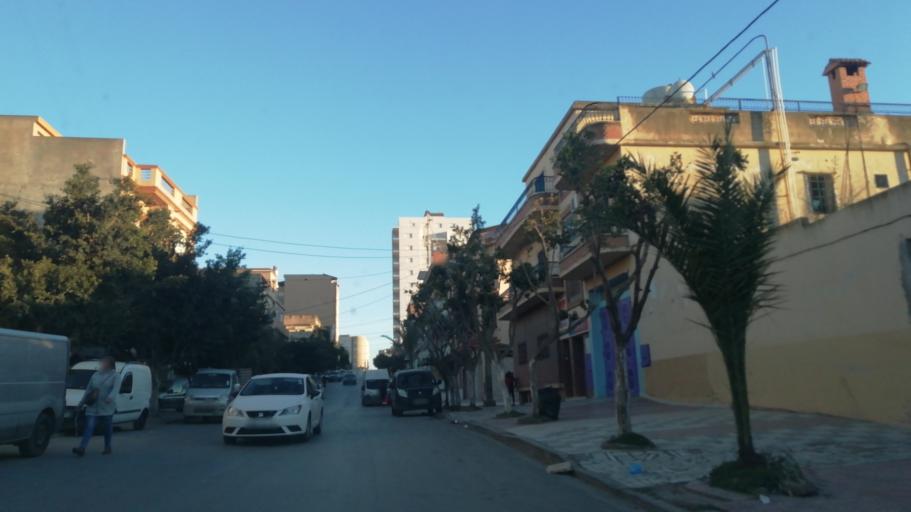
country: DZ
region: Oran
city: Bir el Djir
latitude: 35.7286
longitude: -0.5794
